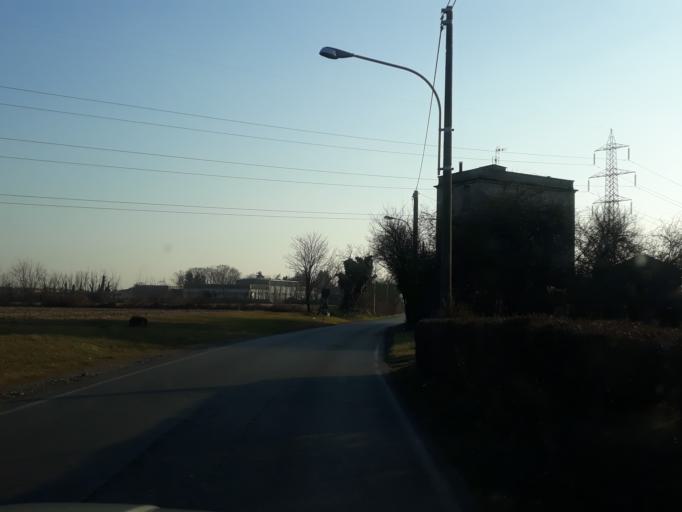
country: IT
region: Lombardy
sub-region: Provincia di Monza e Brianza
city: Bellusco
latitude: 45.6289
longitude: 9.4184
